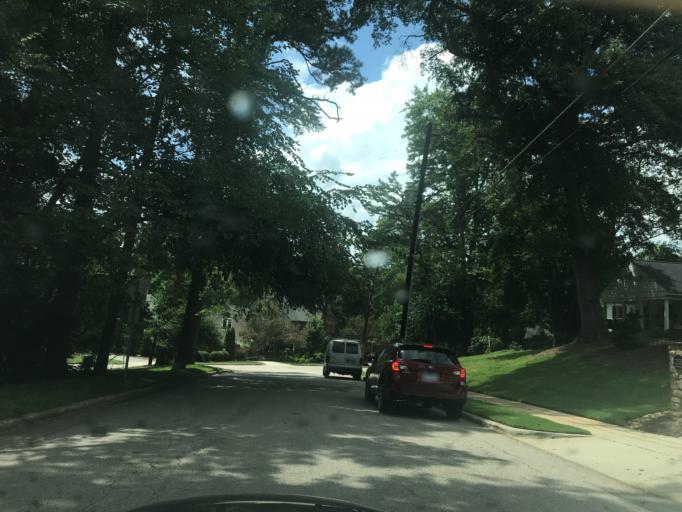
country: US
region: North Carolina
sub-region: Wake County
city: West Raleigh
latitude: 35.8119
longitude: -78.6384
